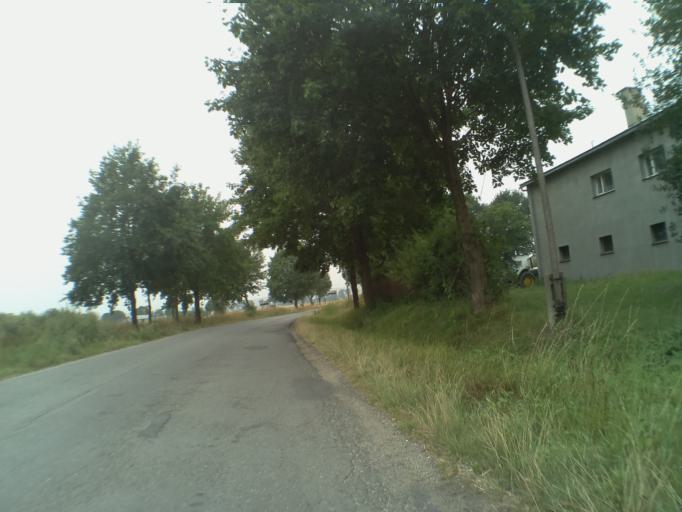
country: PL
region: Lower Silesian Voivodeship
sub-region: Powiat swidnicki
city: Swiebodzice
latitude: 50.8978
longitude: 16.3210
